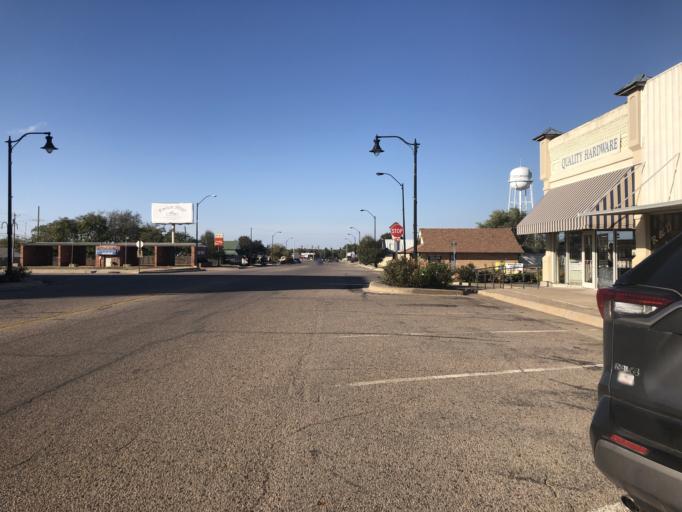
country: US
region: Oklahoma
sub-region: Pottawatomie County
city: Tecumseh
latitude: 35.2584
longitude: -96.9367
